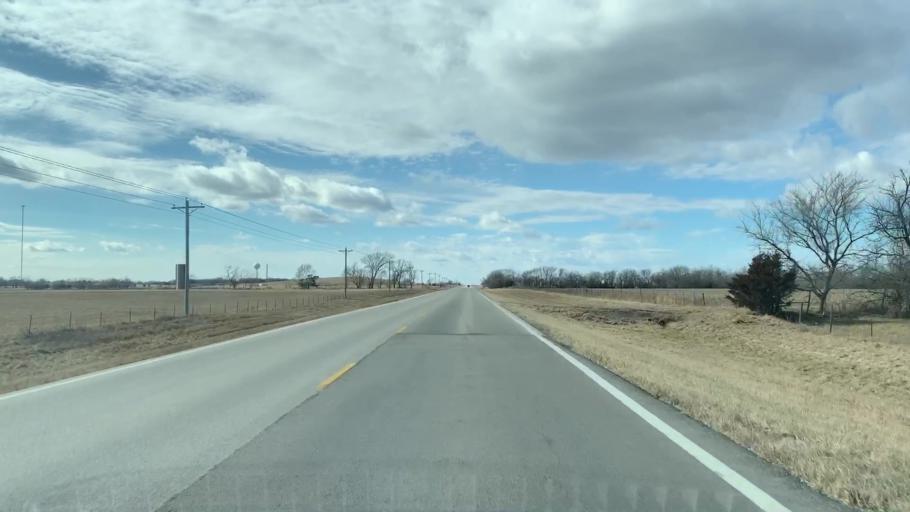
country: US
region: Kansas
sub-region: Neosho County
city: Erie
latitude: 37.5294
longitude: -95.3464
